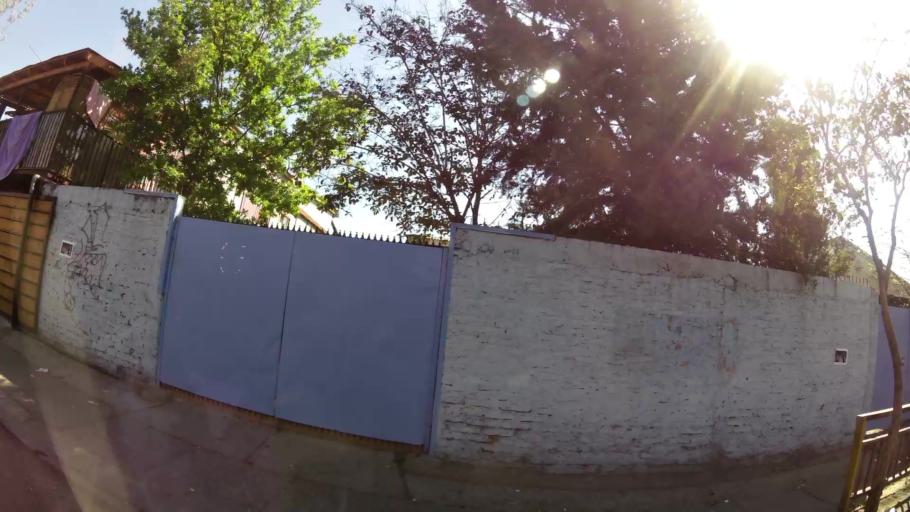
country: CL
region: Santiago Metropolitan
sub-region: Provincia de Santiago
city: La Pintana
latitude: -33.5599
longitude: -70.6272
